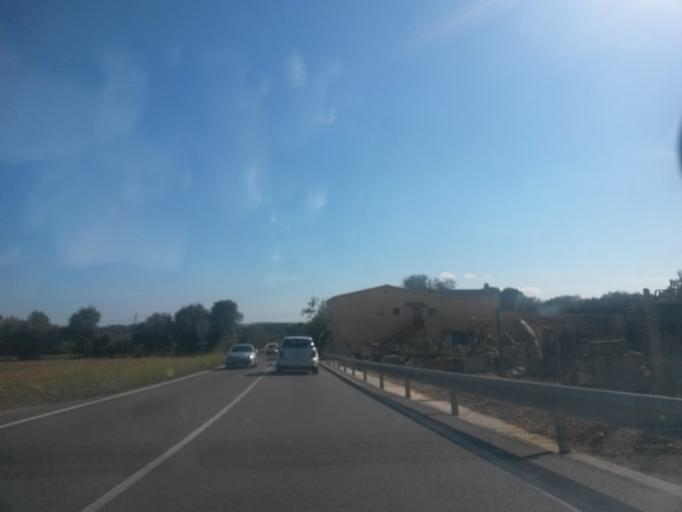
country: ES
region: Catalonia
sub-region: Provincia de Girona
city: Regencos
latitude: 41.9502
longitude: 3.1666
